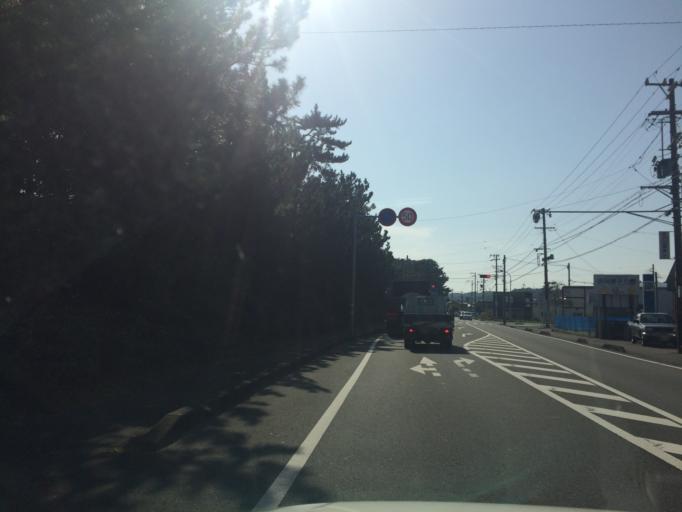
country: JP
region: Shizuoka
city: Sagara
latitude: 34.6779
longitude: 138.1995
